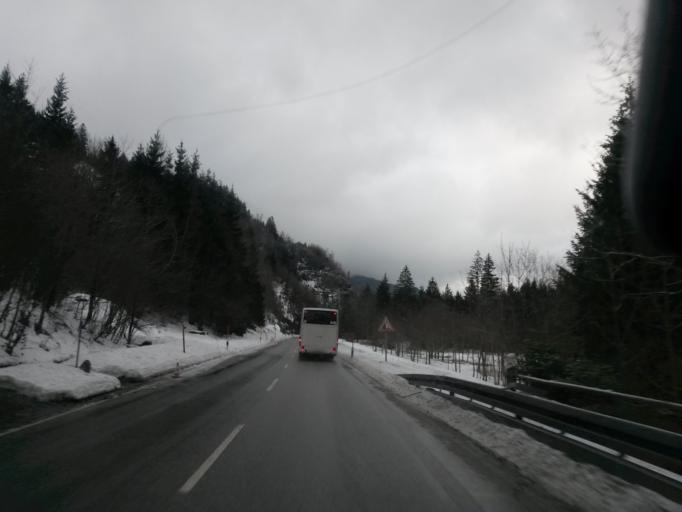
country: DE
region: Bavaria
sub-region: Swabia
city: Wertach
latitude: 47.5824
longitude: 10.4145
